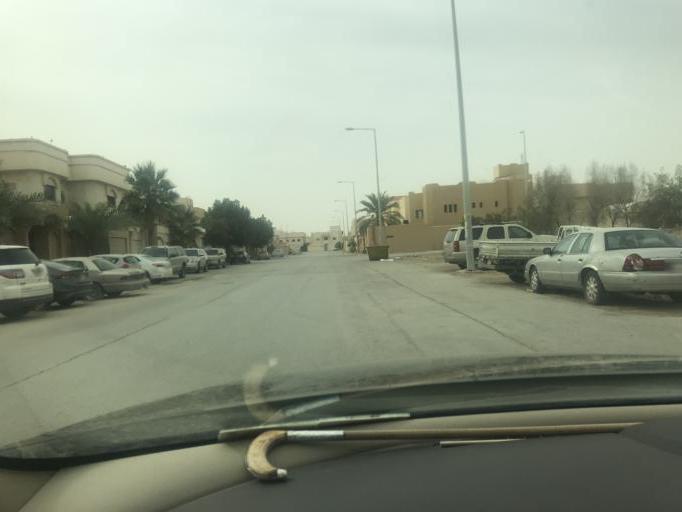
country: SA
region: Ar Riyad
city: Riyadh
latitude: 24.7536
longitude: 46.7637
